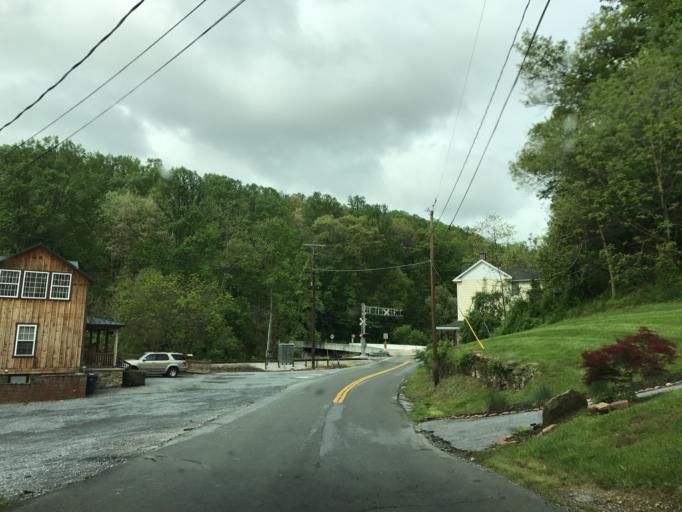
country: US
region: Maryland
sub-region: Carroll County
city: Hampstead
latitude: 39.5389
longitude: -76.8939
